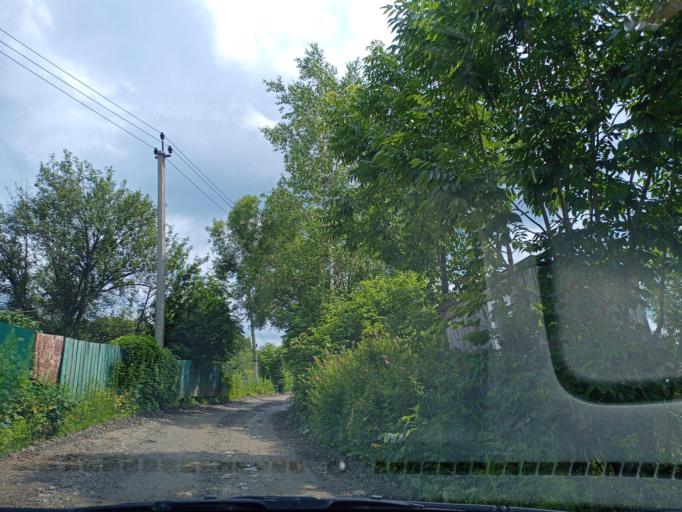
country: RU
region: Khabarovsk Krai
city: Korfovskiy
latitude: 48.3185
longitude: 135.1050
